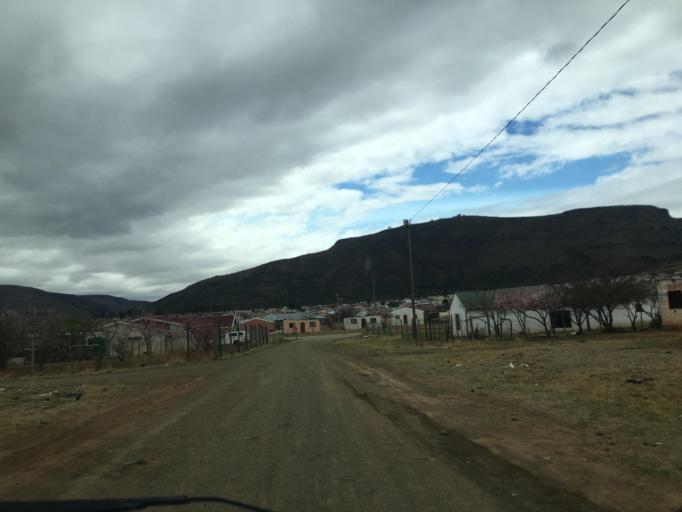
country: ZA
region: Eastern Cape
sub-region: Chris Hani District Municipality
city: Cala
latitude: -31.5391
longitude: 27.6987
